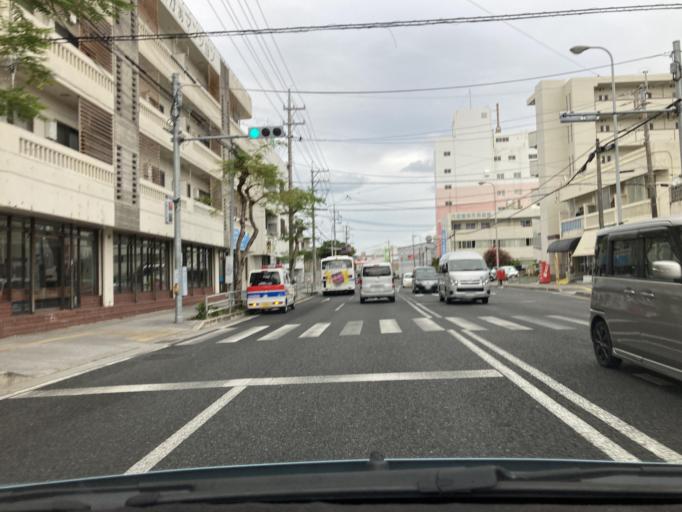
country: JP
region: Okinawa
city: Tomigusuku
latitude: 26.1950
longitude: 127.6761
